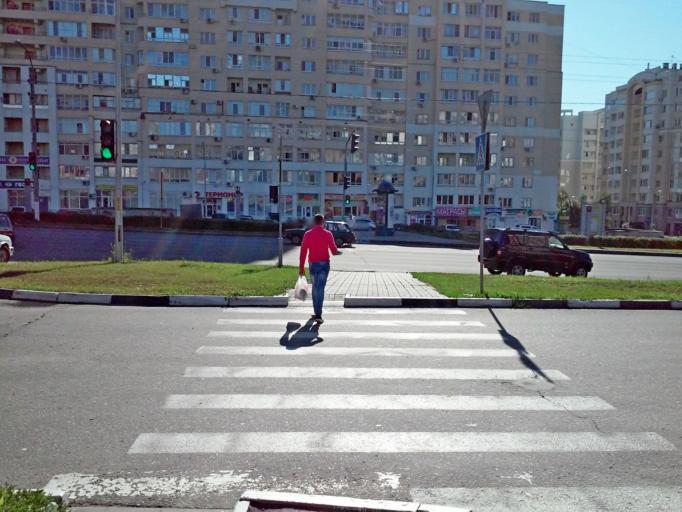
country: RU
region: Belgorod
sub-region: Belgorodskiy Rayon
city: Belgorod
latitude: 50.5602
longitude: 36.5712
